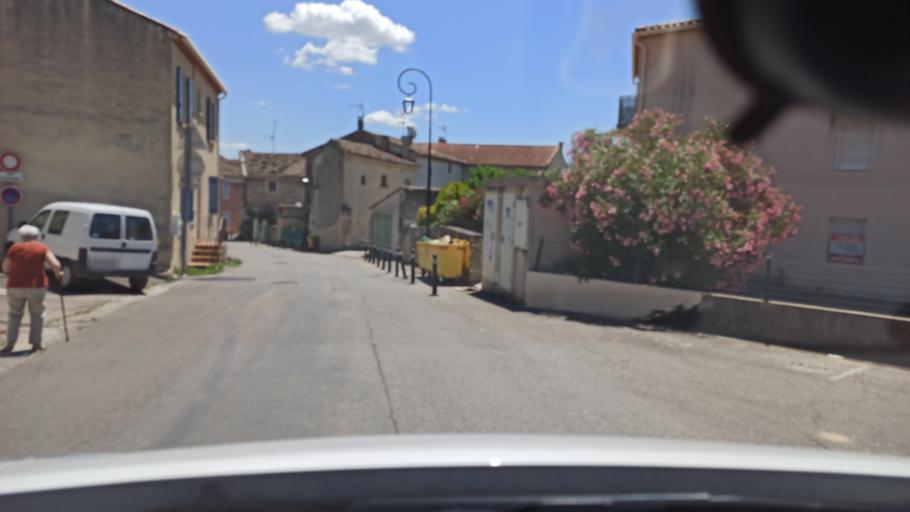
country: FR
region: Provence-Alpes-Cote d'Azur
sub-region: Departement du Vaucluse
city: Caumont-sur-Durance
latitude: 43.8941
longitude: 4.9434
